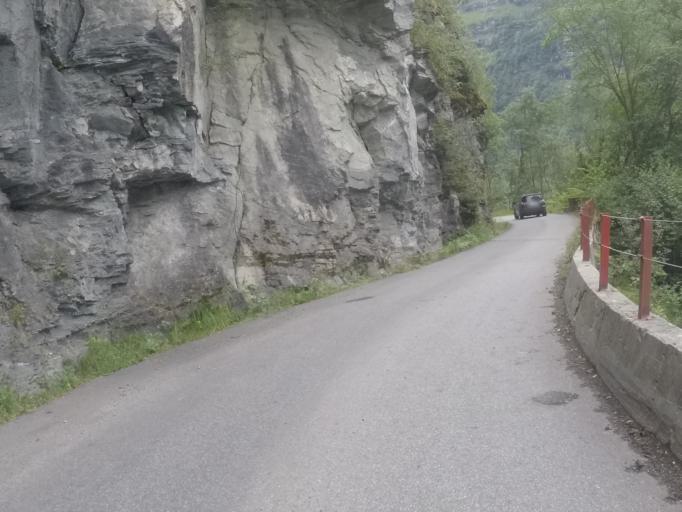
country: NO
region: Sogn og Fjordane
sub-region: Stryn
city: Stryn
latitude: 61.7891
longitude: 6.9987
